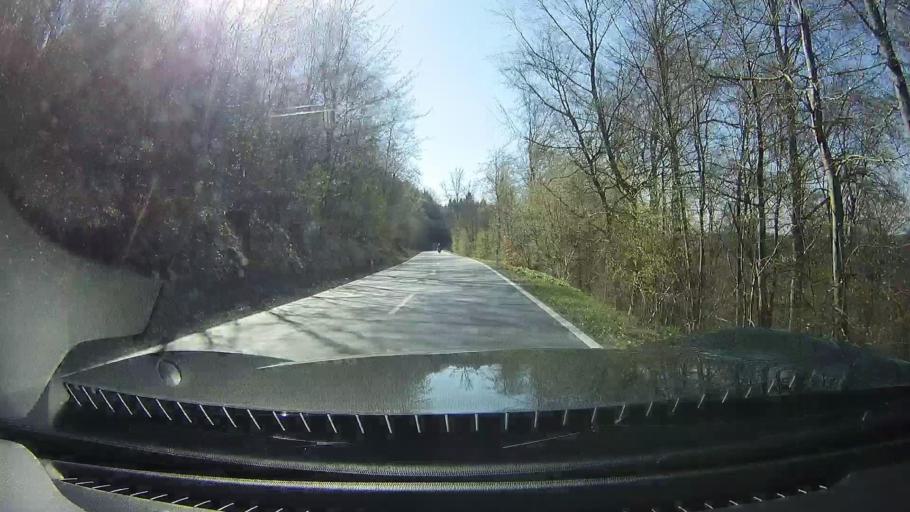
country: DE
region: Baden-Wuerttemberg
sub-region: Karlsruhe Region
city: Eberbach
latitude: 49.4334
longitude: 8.9719
